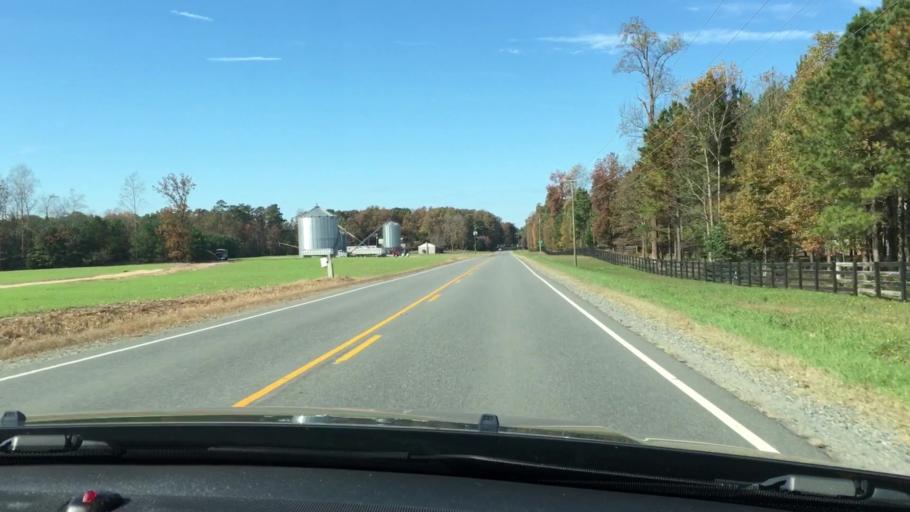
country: US
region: Virginia
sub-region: King and Queen County
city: King and Queen Court House
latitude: 37.5933
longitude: -76.8998
